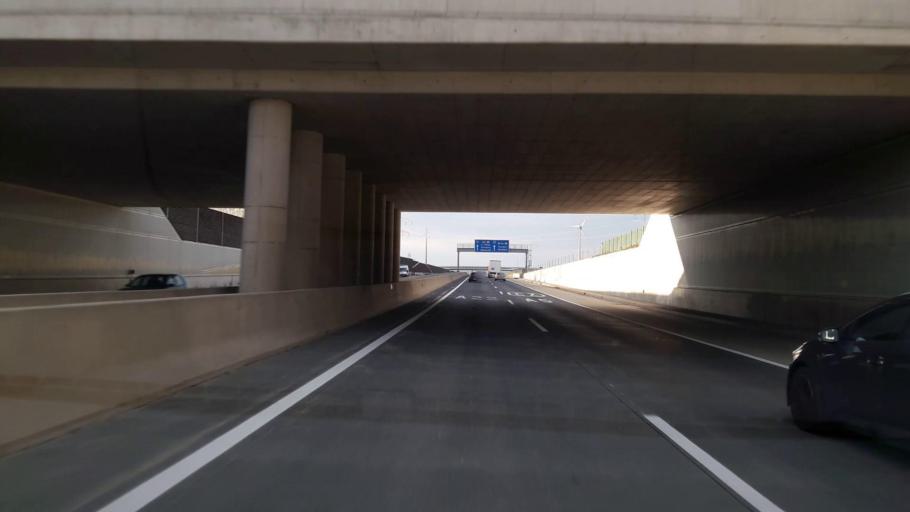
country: AT
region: Lower Austria
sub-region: Politischer Bezirk Mistelbach
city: Pillichsdorf
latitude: 48.3390
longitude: 16.5056
